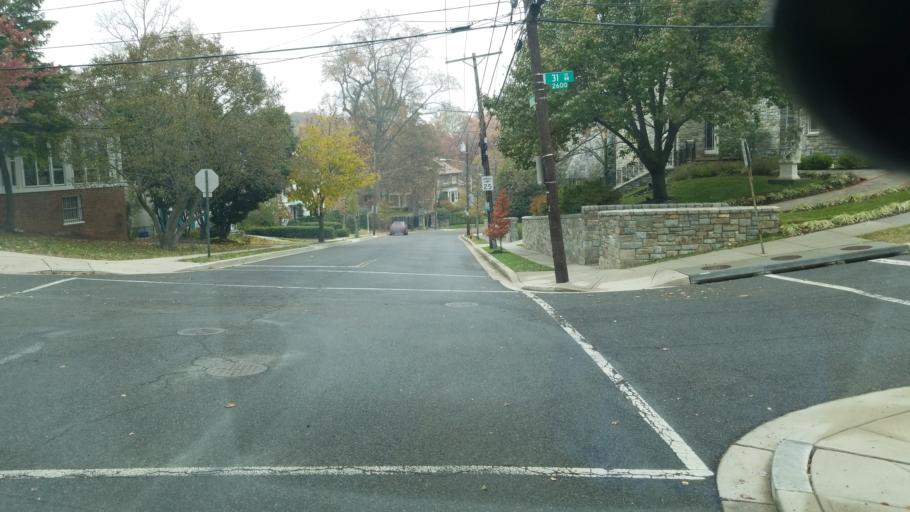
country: US
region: Washington, D.C.
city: Washington, D.C.
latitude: 38.9247
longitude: -77.0619
